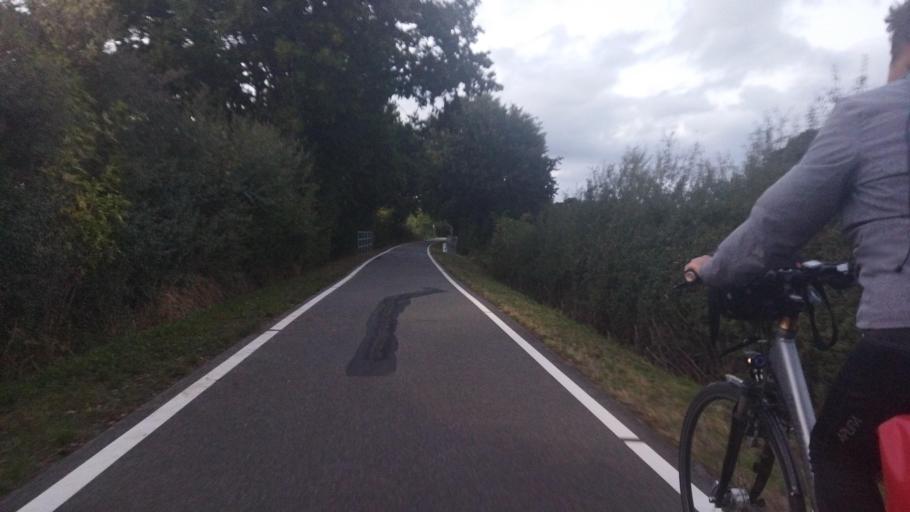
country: DE
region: North Rhine-Westphalia
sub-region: Regierungsbezirk Munster
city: Horstmar
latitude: 52.0802
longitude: 7.3213
